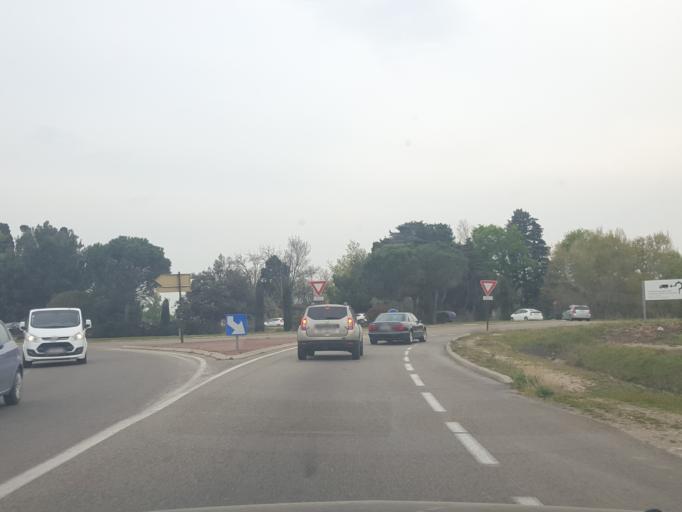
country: FR
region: Provence-Alpes-Cote d'Azur
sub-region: Departement du Vaucluse
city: Vedene
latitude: 43.9784
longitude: 4.8870
